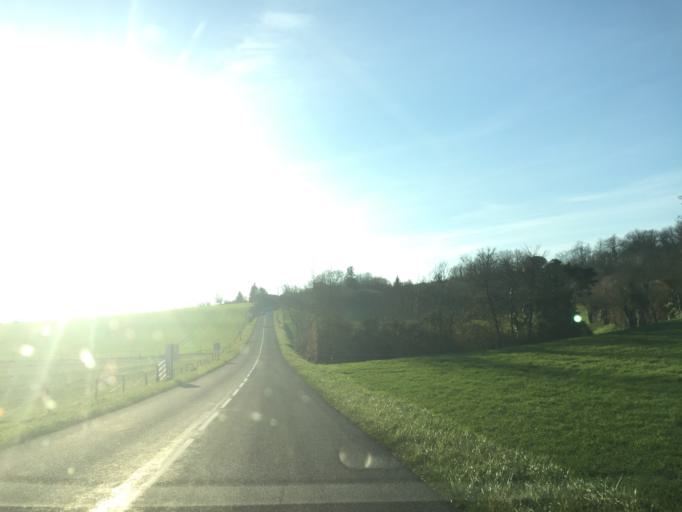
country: FR
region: Aquitaine
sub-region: Departement de la Dordogne
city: Saint-Aulaye
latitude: 45.2709
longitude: 0.1661
